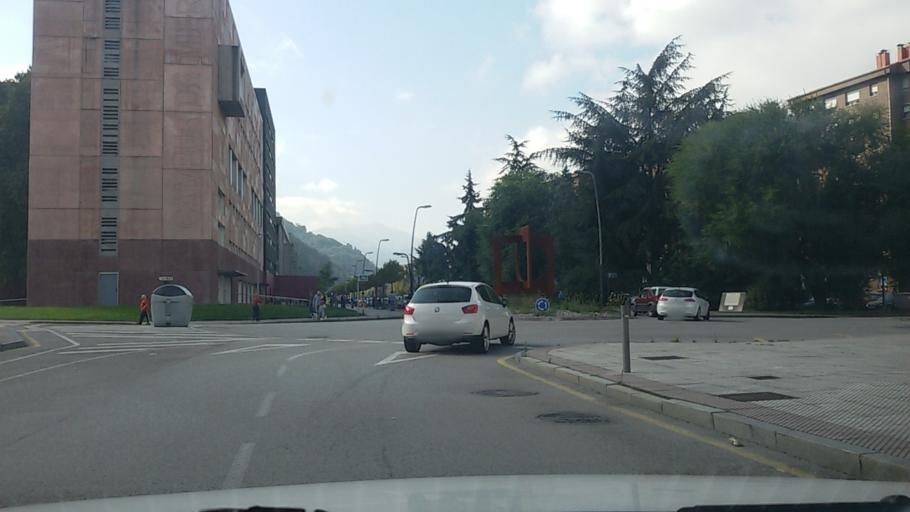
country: ES
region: Asturias
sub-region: Province of Asturias
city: Mieres
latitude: 43.2448
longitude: -5.7767
